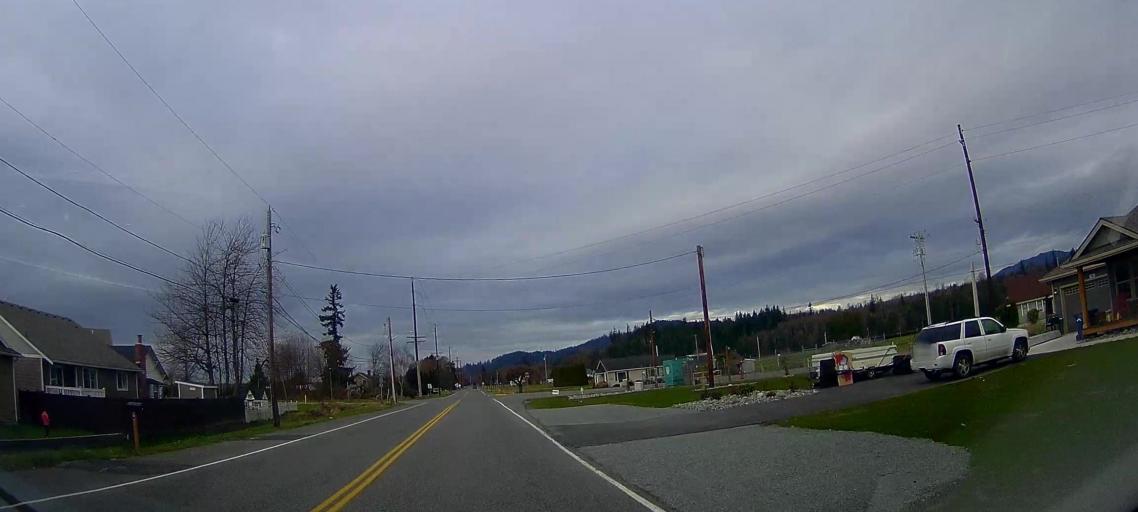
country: US
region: Washington
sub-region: Skagit County
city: Sedro-Woolley
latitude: 48.5142
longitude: -122.2537
